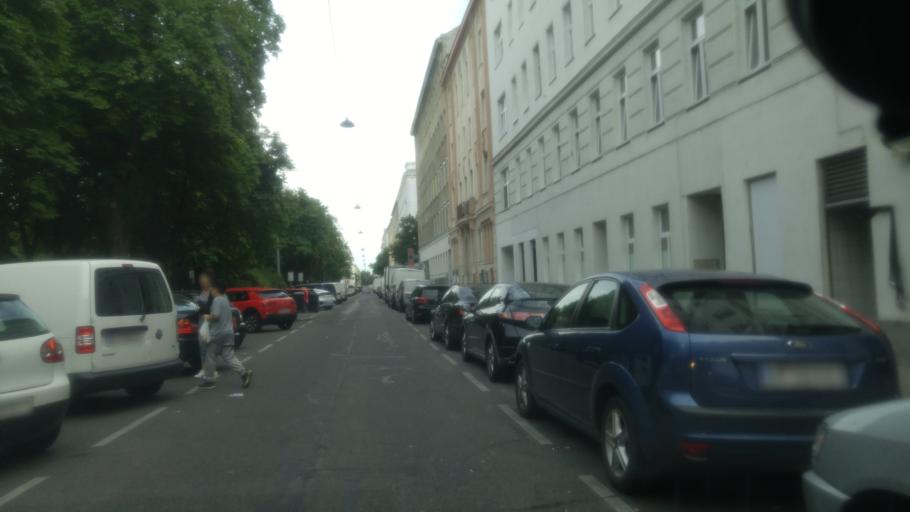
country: AT
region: Vienna
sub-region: Wien Stadt
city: Vienna
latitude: 48.2387
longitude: 16.3835
